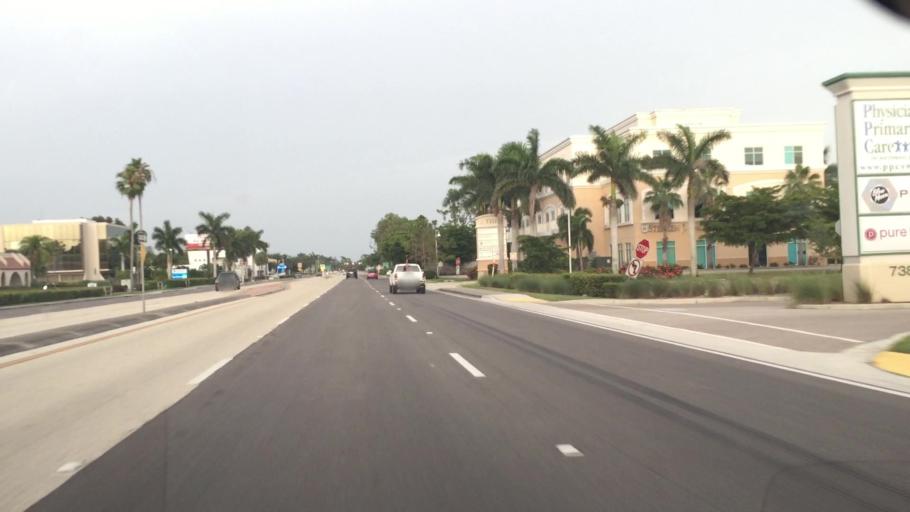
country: US
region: Florida
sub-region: Lee County
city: Villas
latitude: 26.5564
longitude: -81.8785
